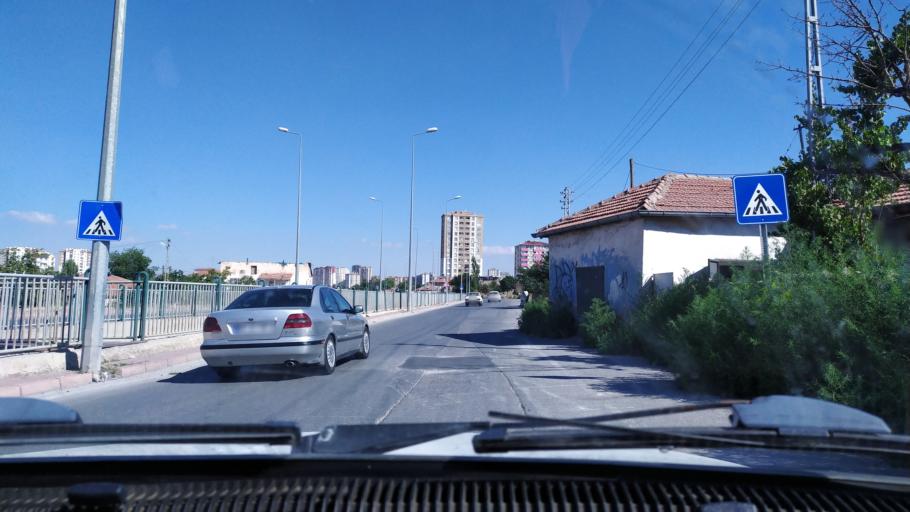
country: TR
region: Kayseri
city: Talas
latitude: 38.7256
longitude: 35.5505
